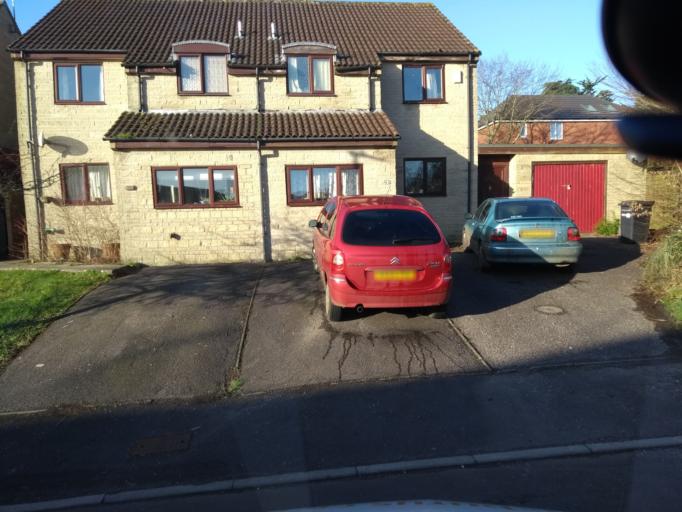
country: GB
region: England
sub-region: Somerset
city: Bruton
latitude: 51.1185
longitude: -2.4481
